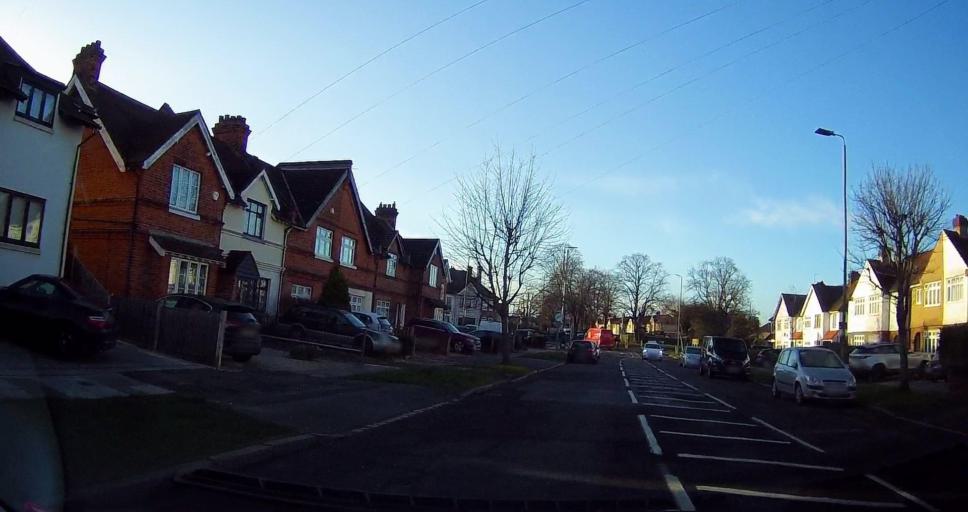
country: GB
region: England
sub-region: Greater London
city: Chislehurst
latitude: 51.3915
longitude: 0.0540
